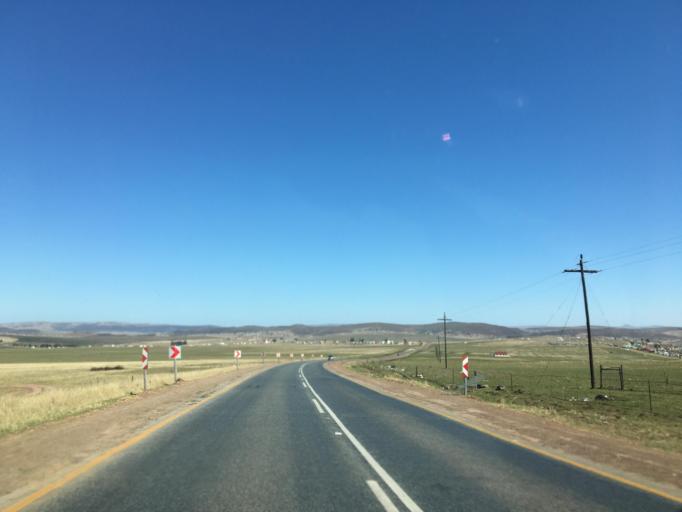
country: ZA
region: Eastern Cape
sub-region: Chris Hani District Municipality
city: Cofimvaba
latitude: -31.9422
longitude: 27.8366
